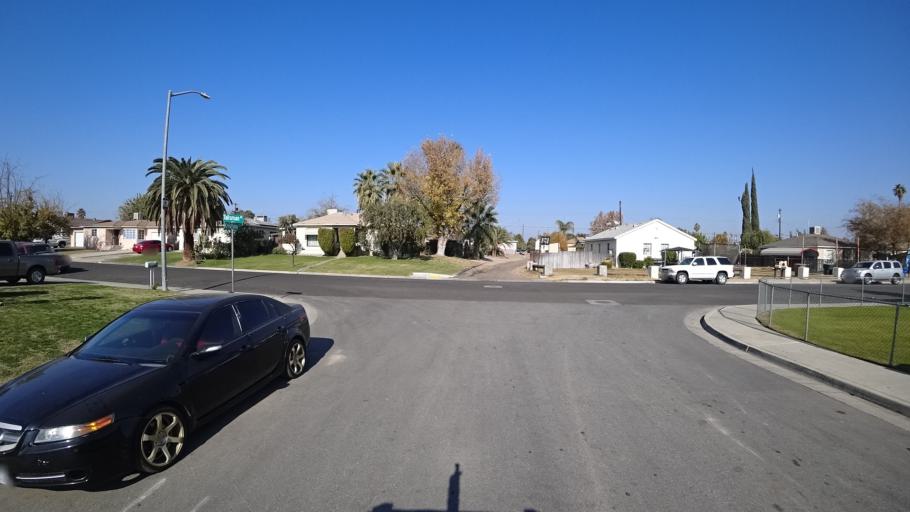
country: US
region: California
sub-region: Kern County
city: Bakersfield
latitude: 35.3411
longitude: -119.0244
